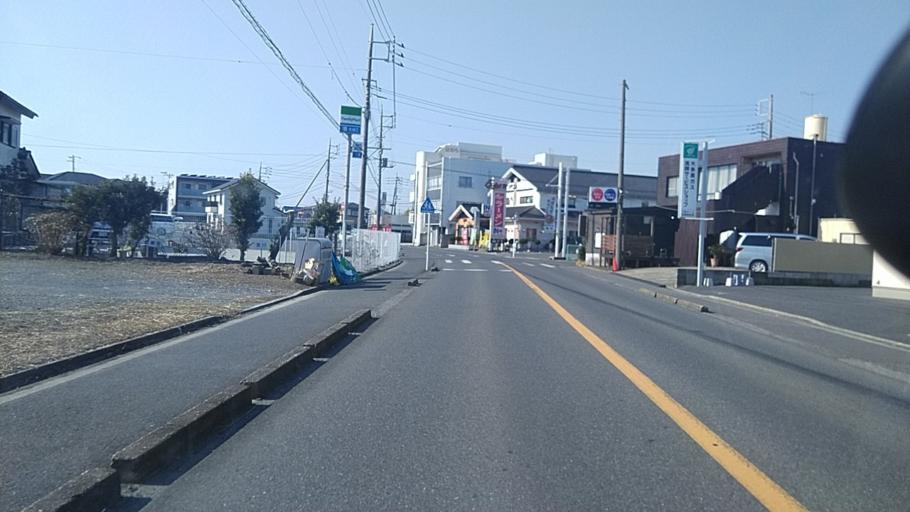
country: JP
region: Chiba
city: Mobara
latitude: 35.4300
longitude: 140.2974
